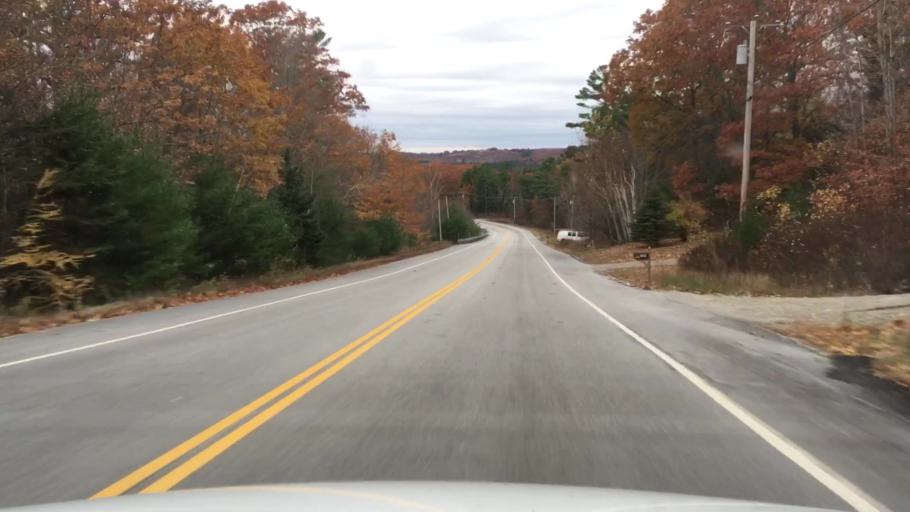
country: US
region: Maine
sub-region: Hancock County
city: Orland
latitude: 44.5556
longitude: -68.6961
